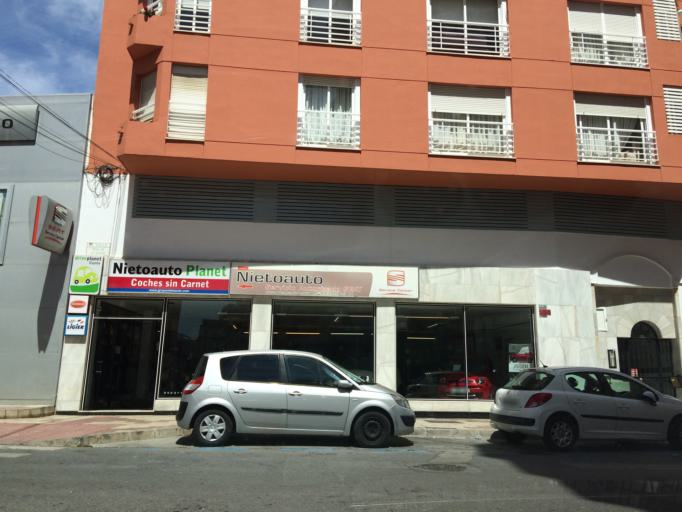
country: ES
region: Andalusia
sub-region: Provincia de Malaga
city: Malaga
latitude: 36.7205
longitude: -4.4313
